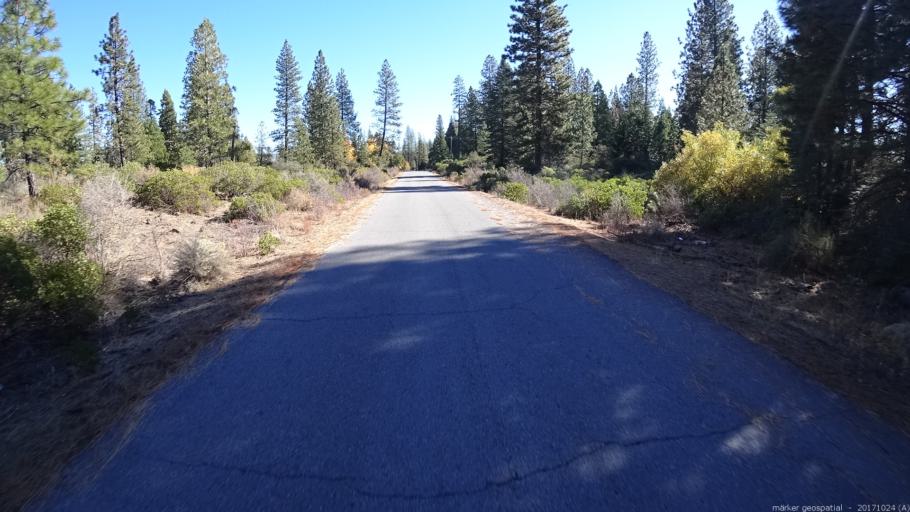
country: US
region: California
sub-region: Shasta County
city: Burney
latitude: 40.7539
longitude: -121.4855
